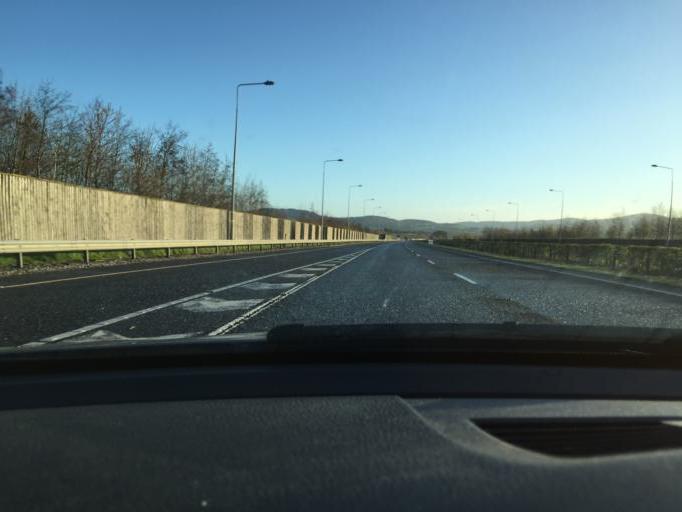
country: IE
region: Leinster
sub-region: Lu
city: Dundalk
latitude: 54.0219
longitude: -6.4406
